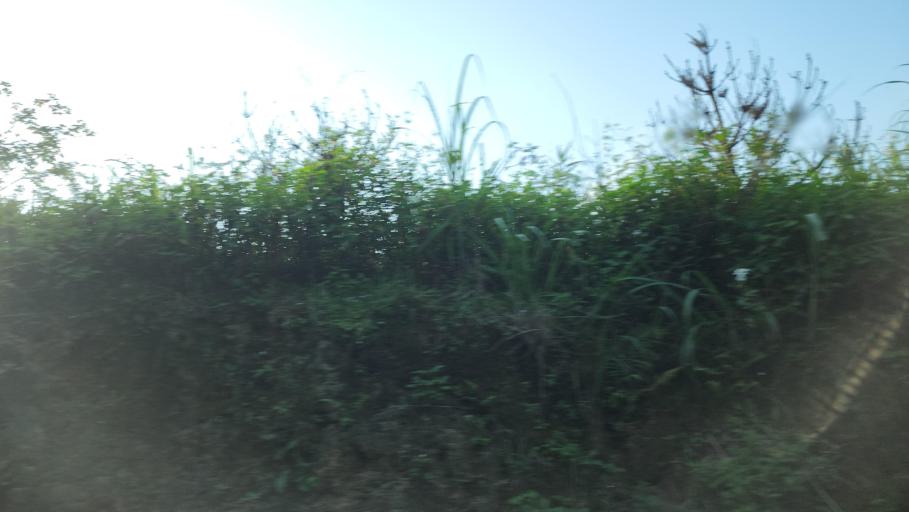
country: TW
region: Taiwan
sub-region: Keelung
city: Keelung
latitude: 25.1783
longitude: 121.6499
